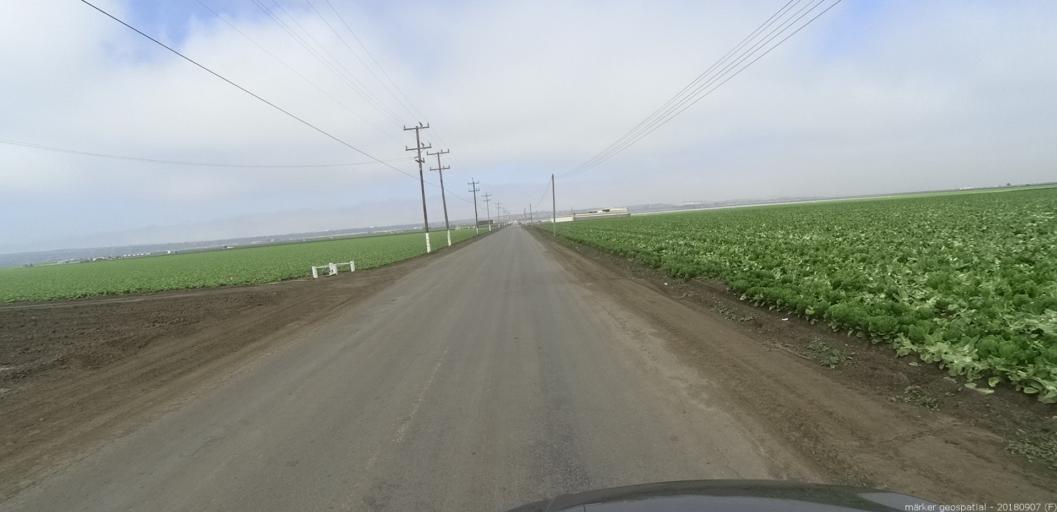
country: US
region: California
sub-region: Monterey County
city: Boronda
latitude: 36.6933
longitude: -121.7165
